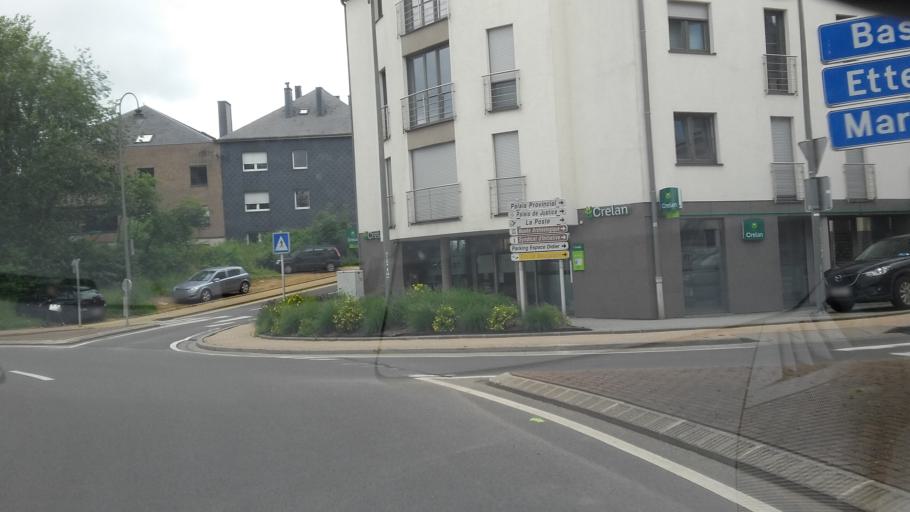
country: BE
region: Wallonia
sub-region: Province du Luxembourg
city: Arlon
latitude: 49.6819
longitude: 5.8060
